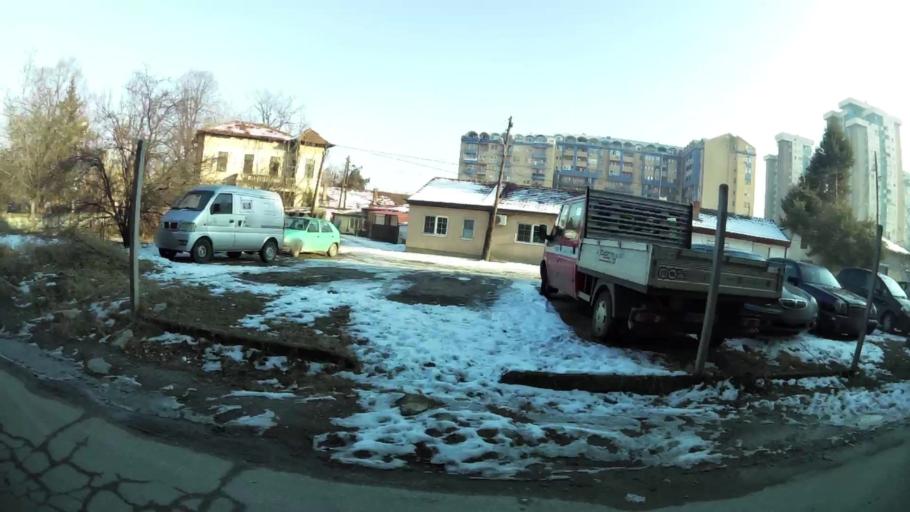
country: MK
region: Karpos
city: Skopje
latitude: 41.9931
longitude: 21.4487
